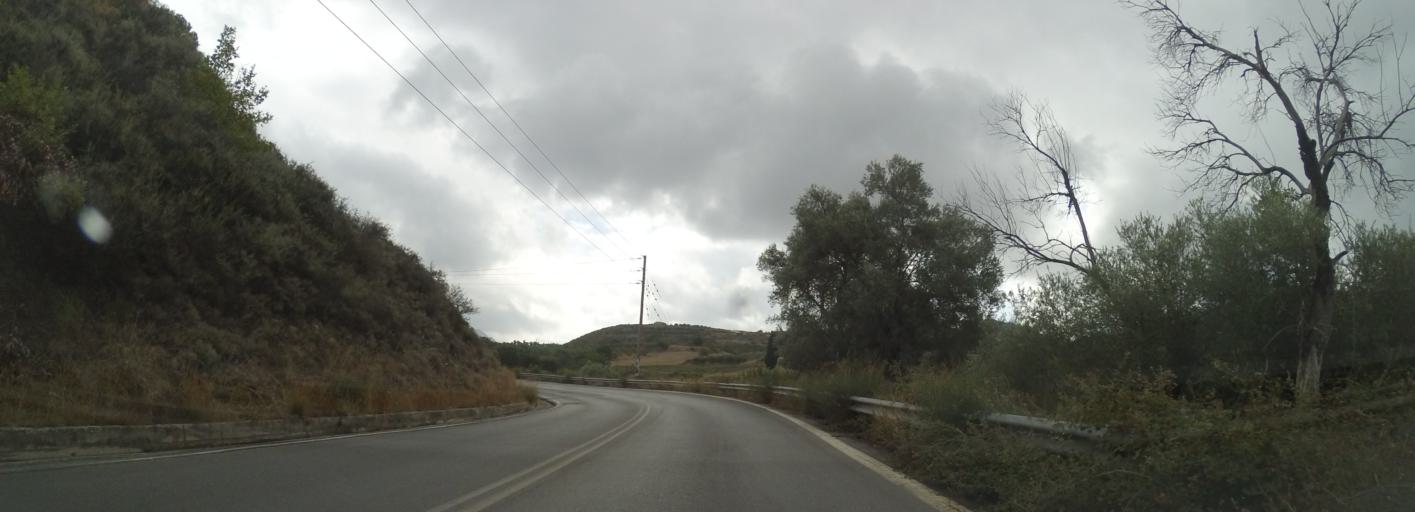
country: GR
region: Crete
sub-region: Nomos Rethymnis
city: Agia Foteini
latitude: 35.2206
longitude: 24.5117
